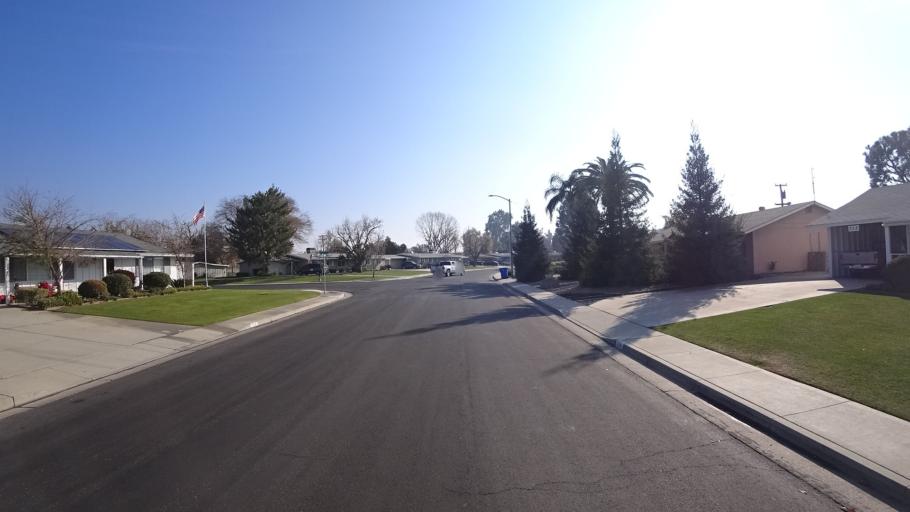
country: US
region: California
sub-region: Kern County
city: Greenacres
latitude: 35.3484
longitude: -119.0713
